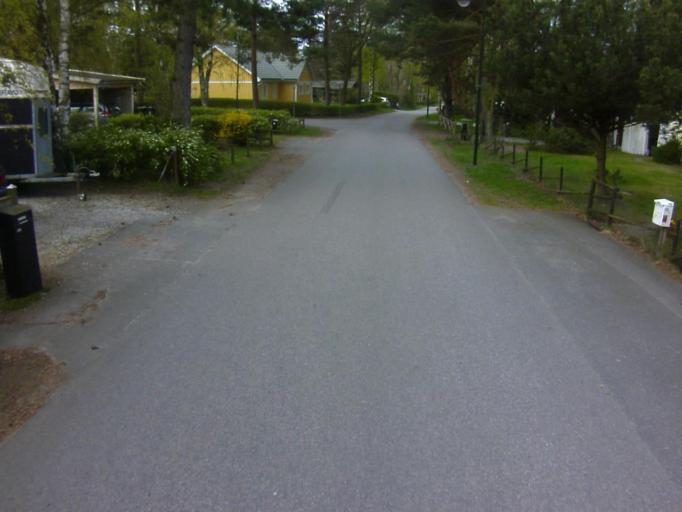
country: SE
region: Skane
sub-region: Kavlinge Kommun
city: Hofterup
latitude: 55.7610
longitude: 12.9768
